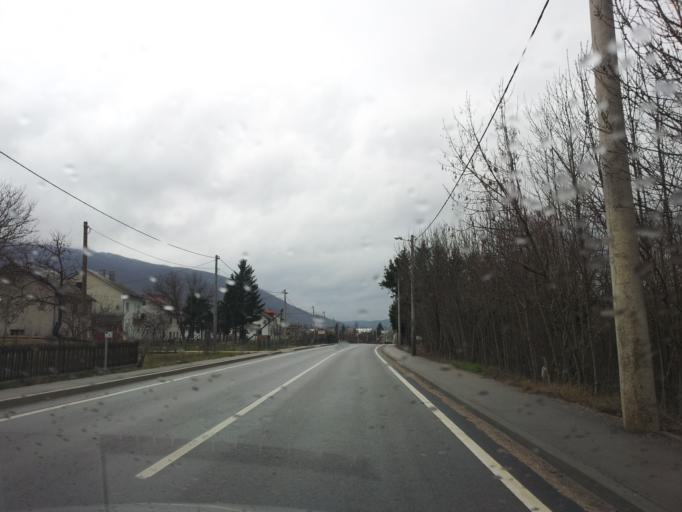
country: BA
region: Federation of Bosnia and Herzegovina
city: Izacic
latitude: 44.7370
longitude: 15.7182
